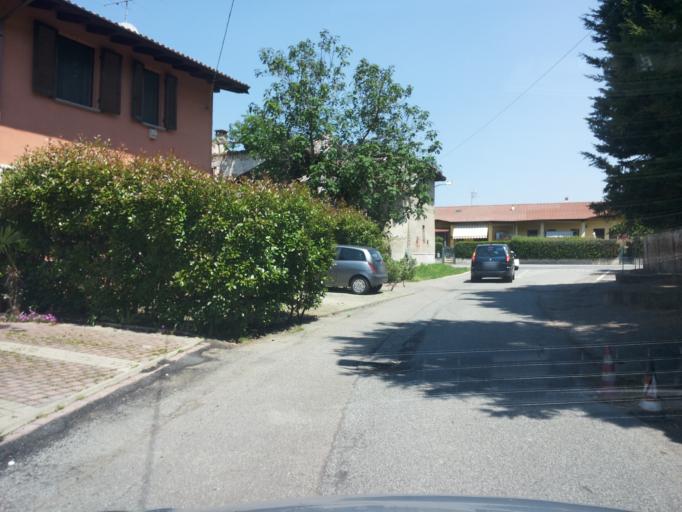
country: IT
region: Piedmont
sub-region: Provincia di Vercelli
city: Borgo Vercelli
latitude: 45.3597
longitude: 8.4675
